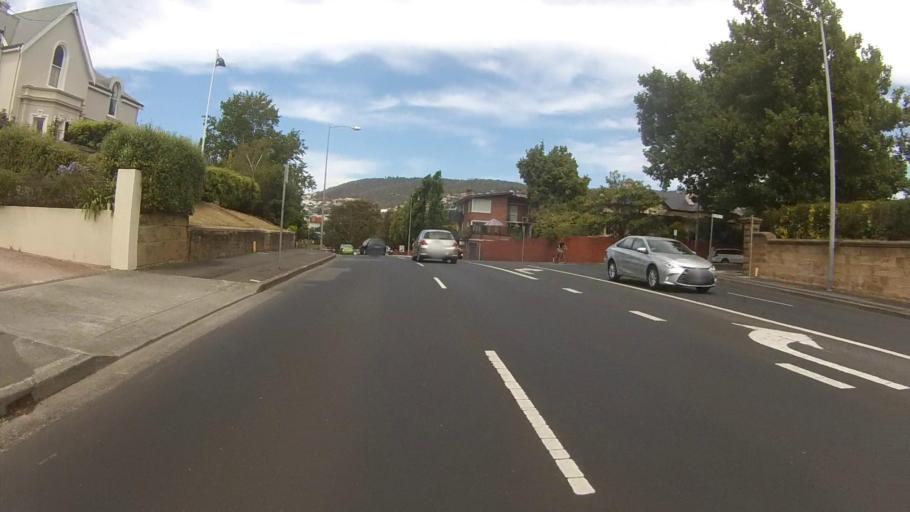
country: AU
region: Tasmania
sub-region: Hobart
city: Sandy Bay
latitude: -42.8979
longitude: 147.3292
